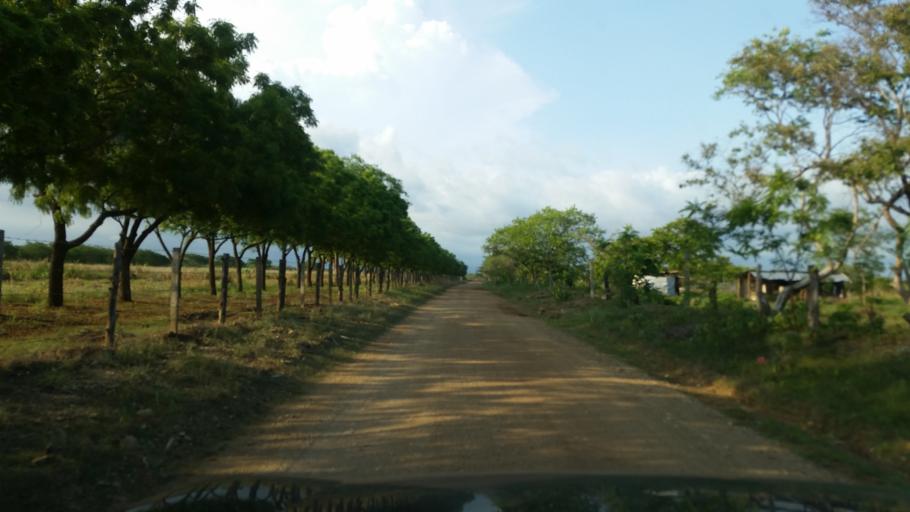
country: NI
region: Managua
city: Masachapa
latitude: 11.7641
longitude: -86.4878
